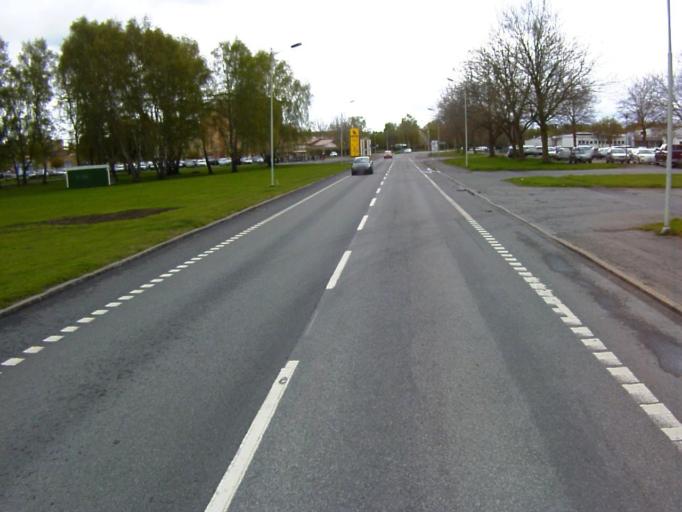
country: SE
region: Skane
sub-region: Kristianstads Kommun
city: Kristianstad
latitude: 56.0443
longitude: 14.1767
